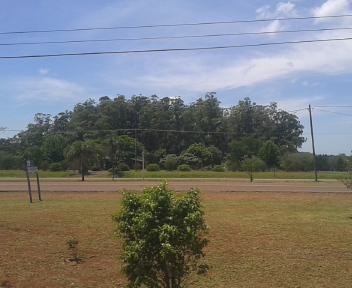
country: AR
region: Misiones
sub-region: Departamento de Leandro N. Alem
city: Leandro N. Alem
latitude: -27.6202
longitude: -55.3342
